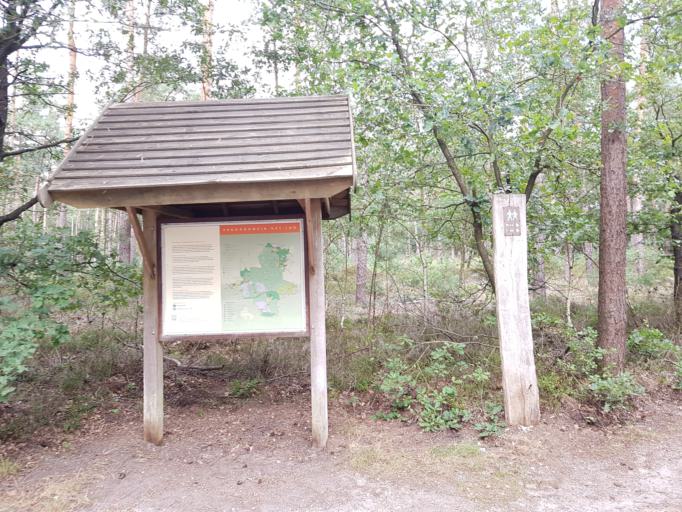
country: NL
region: Gelderland
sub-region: Gemeente Apeldoorn
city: Uddel
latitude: 52.2531
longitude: 5.8063
